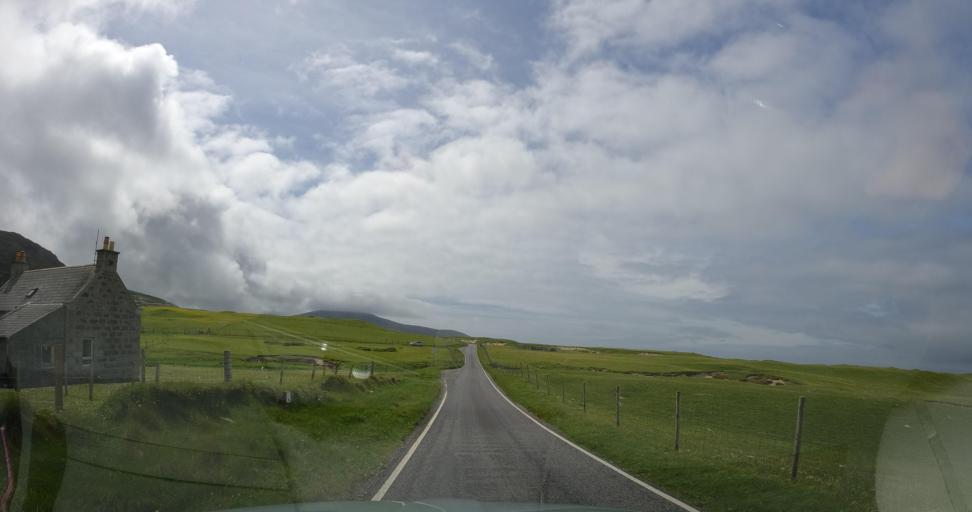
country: GB
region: Scotland
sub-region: Eilean Siar
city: Barra
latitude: 57.0011
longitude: -7.5023
